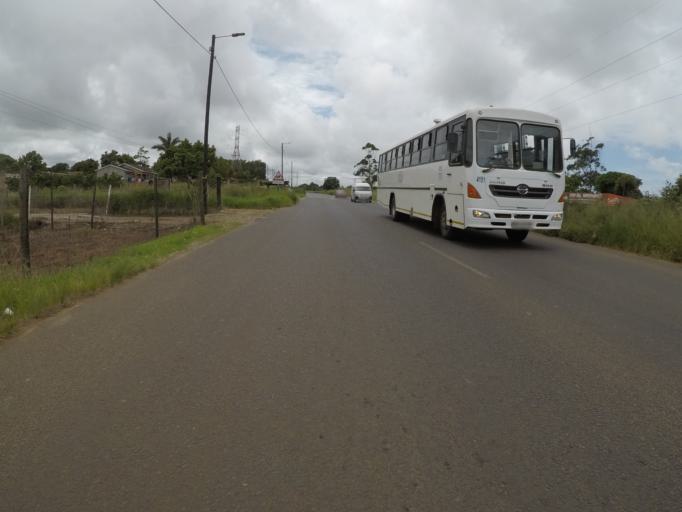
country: ZA
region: KwaZulu-Natal
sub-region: uThungulu District Municipality
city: eSikhawini
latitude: -28.8468
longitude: 31.9306
